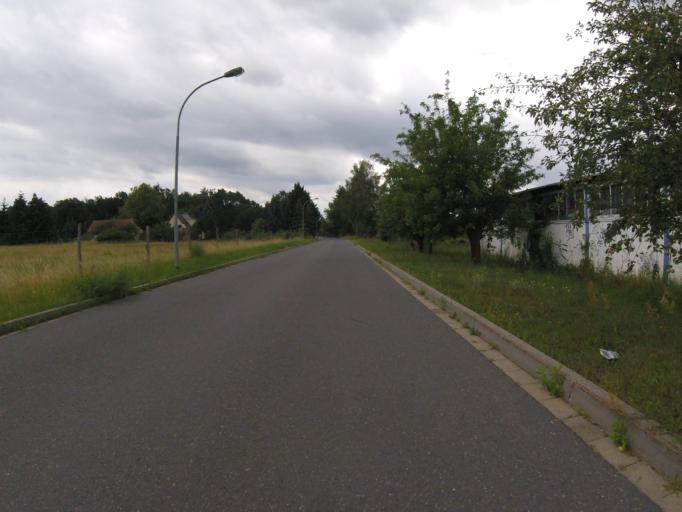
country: DE
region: Brandenburg
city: Konigs Wusterhausen
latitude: 52.3020
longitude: 13.6389
